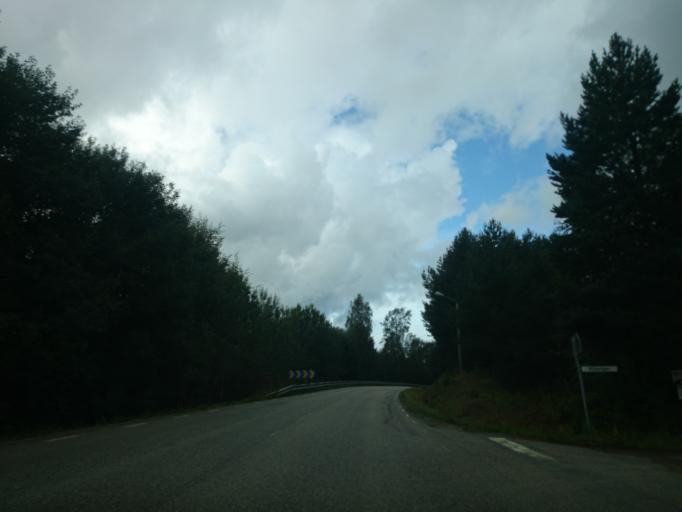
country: SE
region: Vaesternorrland
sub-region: Sundsvalls Kommun
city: Vi
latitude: 62.3098
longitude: 17.1813
